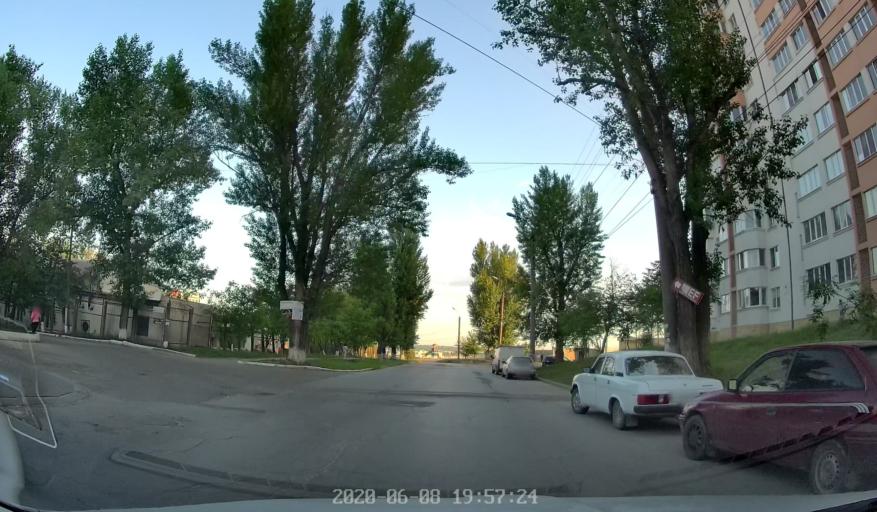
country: MD
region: Chisinau
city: Chisinau
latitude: 47.0161
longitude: 28.8825
